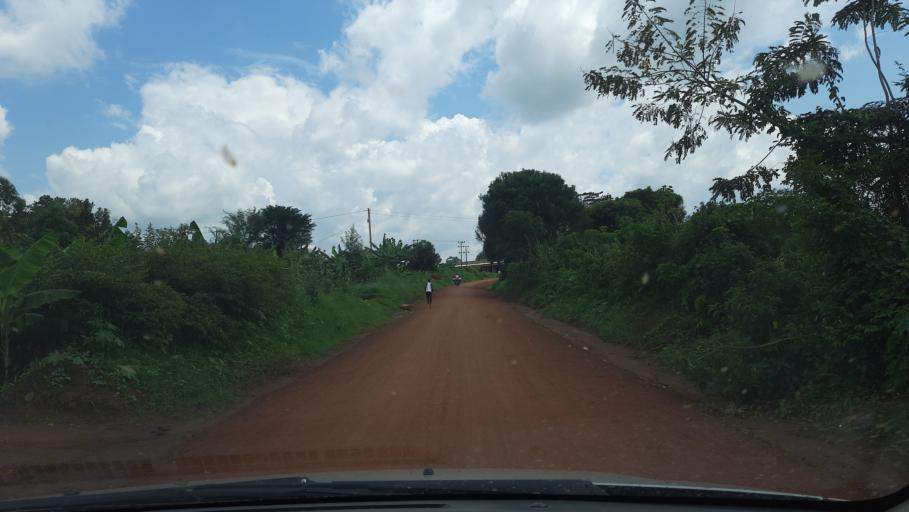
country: UG
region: Western Region
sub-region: Kiryandongo District
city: Kiryandongo
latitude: 1.8141
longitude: 31.9961
